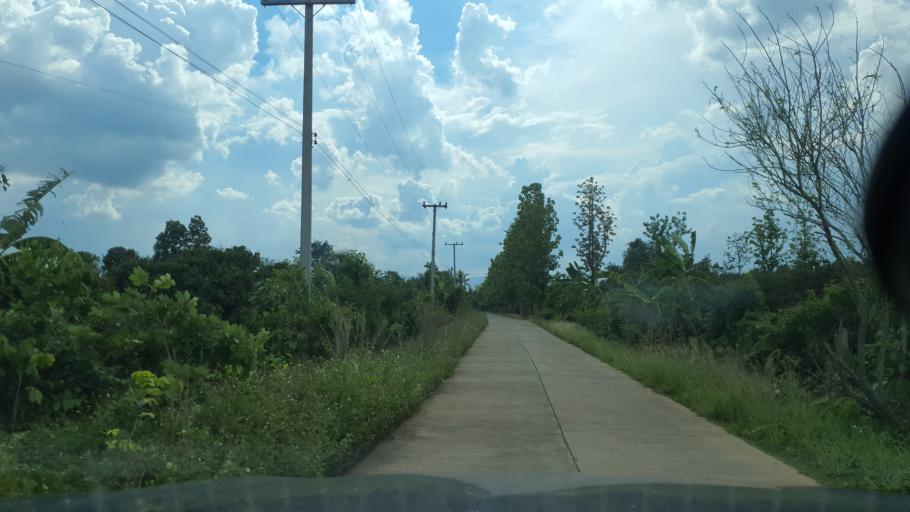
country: TH
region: Chiang Mai
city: Mae Taeng
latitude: 19.1319
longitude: 99.0361
